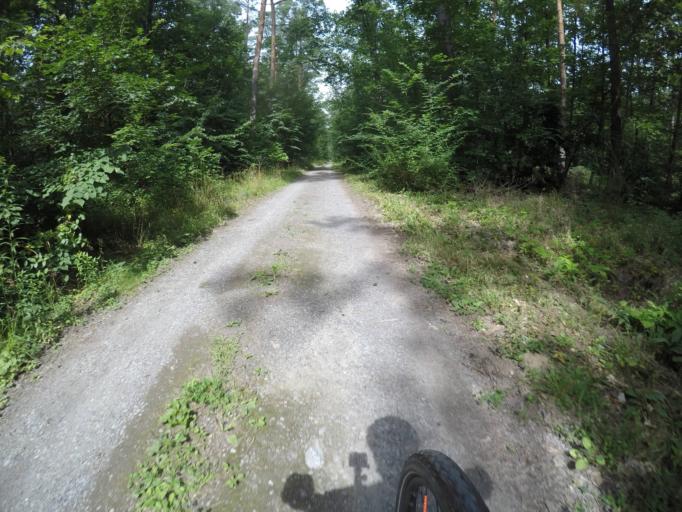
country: DE
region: Baden-Wuerttemberg
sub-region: Karlsruhe Region
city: Hambrucken
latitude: 49.2024
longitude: 8.5483
